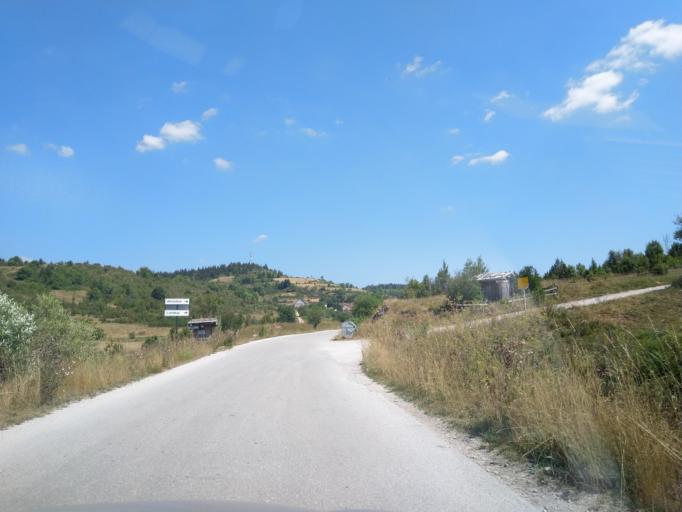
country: RS
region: Central Serbia
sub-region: Zlatiborski Okrug
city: Nova Varos
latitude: 43.4508
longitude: 19.9677
